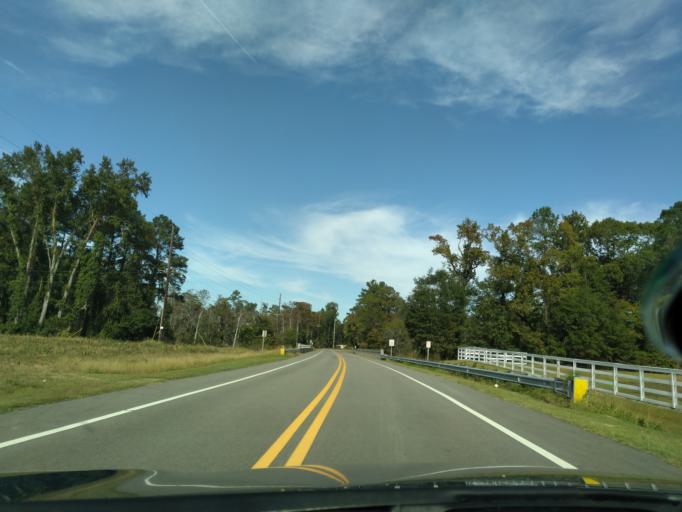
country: US
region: North Carolina
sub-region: Beaufort County
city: River Road
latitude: 35.5100
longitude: -76.9664
